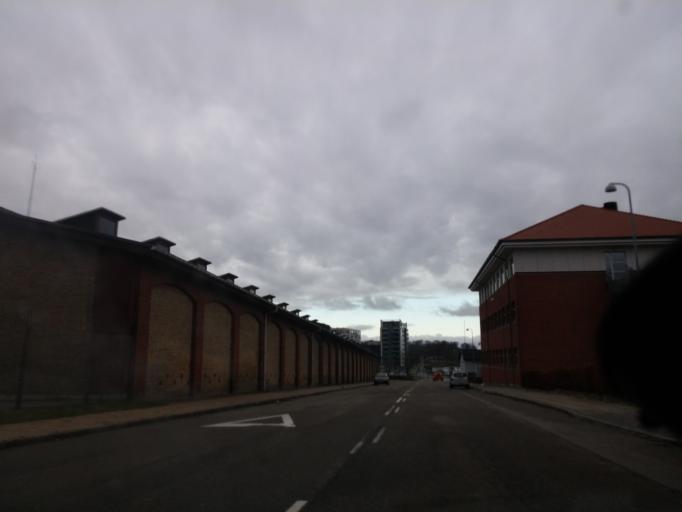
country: DK
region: South Denmark
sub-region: Odense Kommune
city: Odense
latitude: 55.4038
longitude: 10.3835
